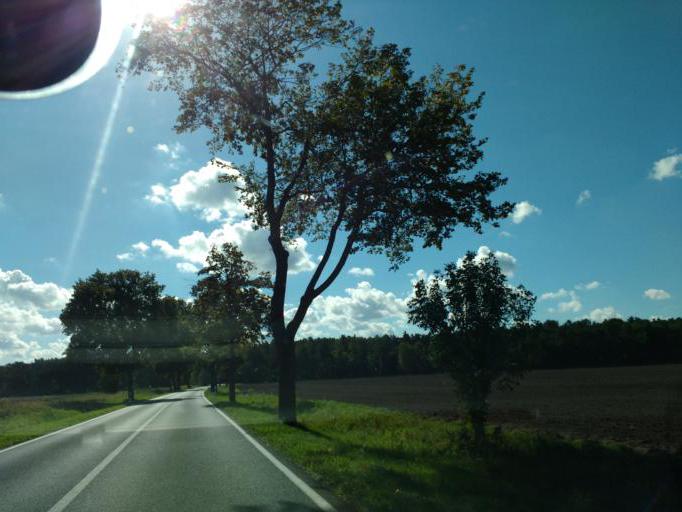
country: DE
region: Brandenburg
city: Mittenwalde
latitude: 52.2287
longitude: 13.5733
